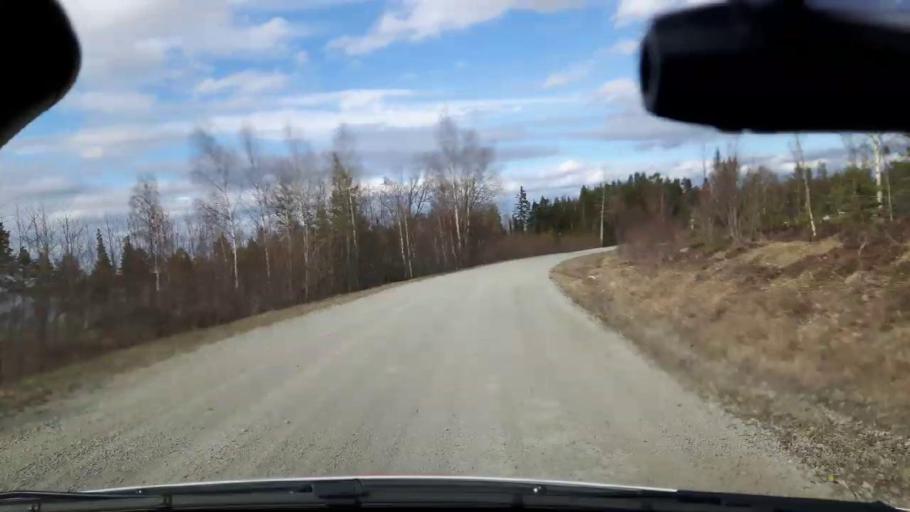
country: SE
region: Jaemtland
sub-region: Bergs Kommun
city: Hoverberg
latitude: 62.7577
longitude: 14.6638
